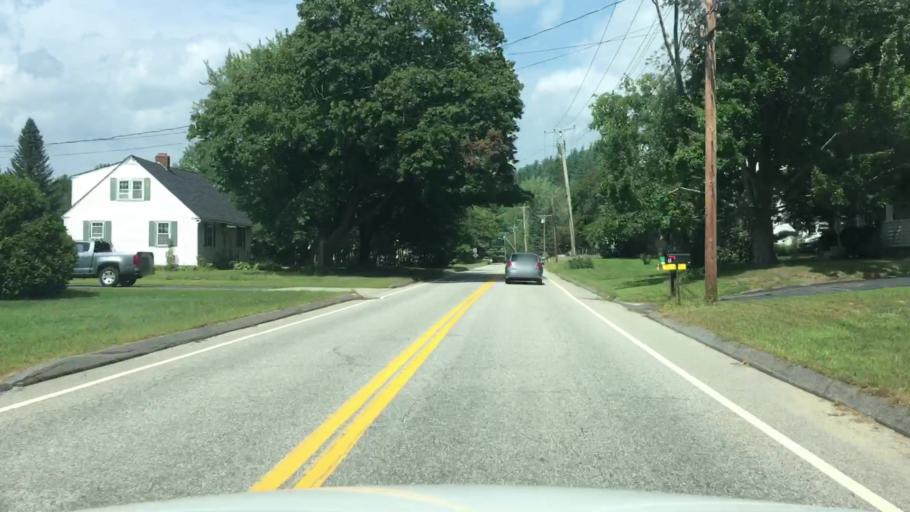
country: US
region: Maine
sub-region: Oxford County
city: Rumford
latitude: 44.5247
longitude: -70.5339
